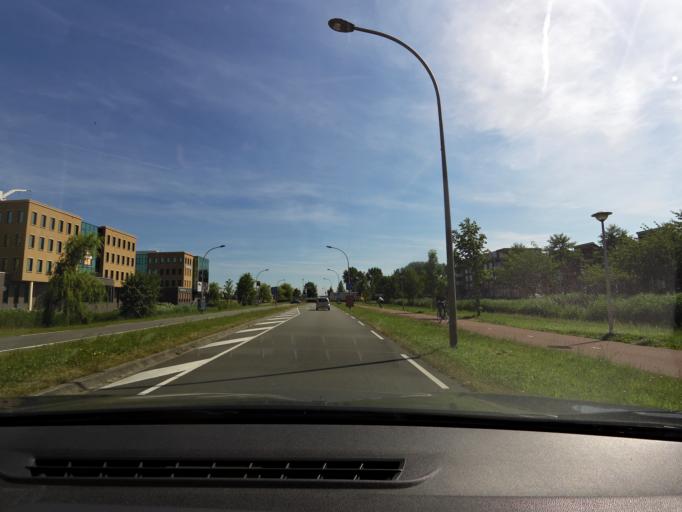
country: NL
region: South Holland
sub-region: Gemeente Barendrecht
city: Barendrecht
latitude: 51.8508
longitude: 4.5083
